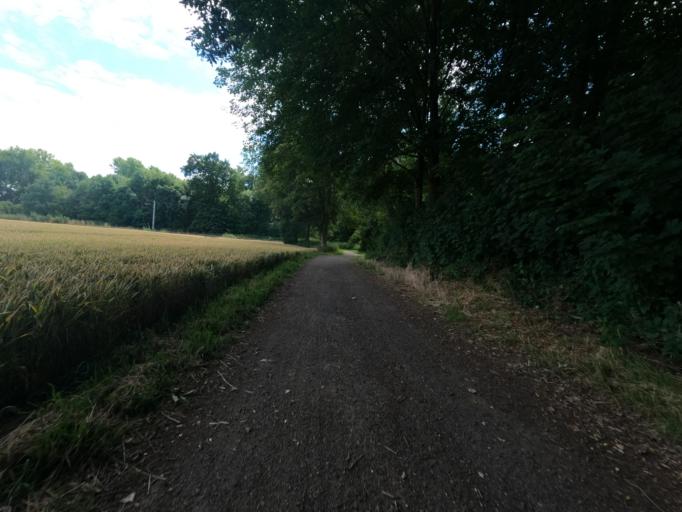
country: DE
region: North Rhine-Westphalia
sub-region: Regierungsbezirk Koln
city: Heinsberg
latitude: 51.0493
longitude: 6.1457
